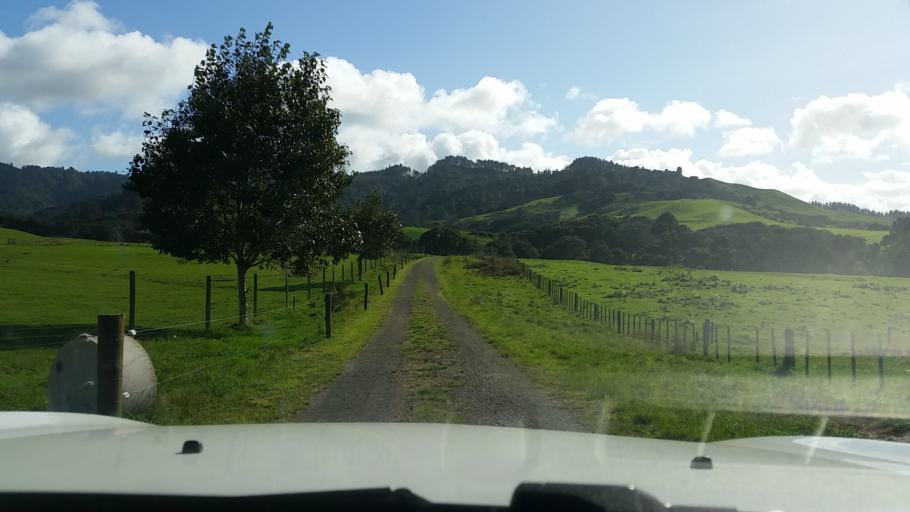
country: NZ
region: Waikato
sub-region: Hauraki District
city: Ngatea
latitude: -37.4983
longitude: 175.4034
